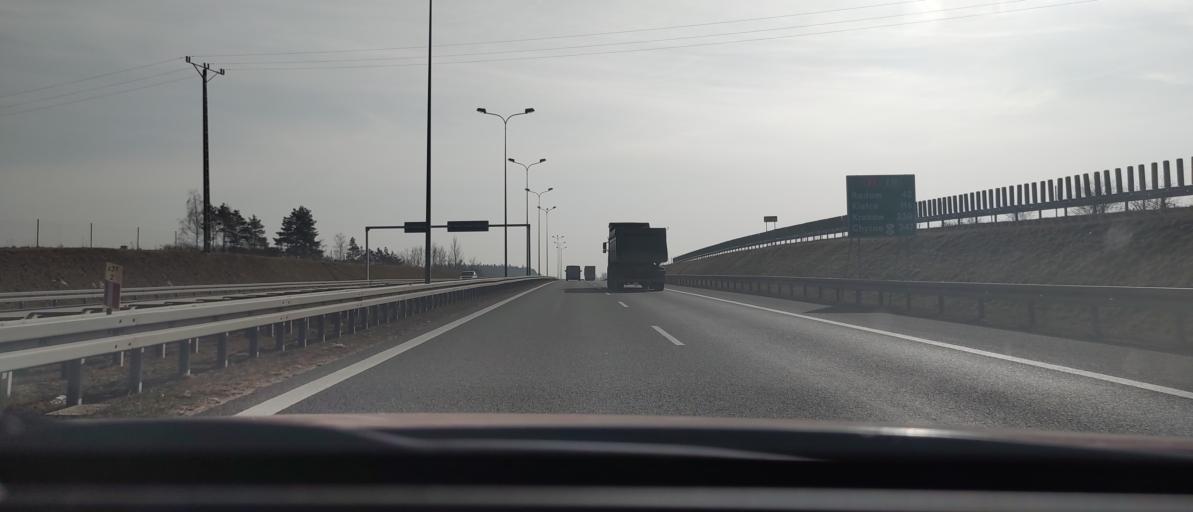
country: PL
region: Masovian Voivodeship
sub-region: Powiat grojecki
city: Goszczyn
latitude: 51.7319
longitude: 20.9156
